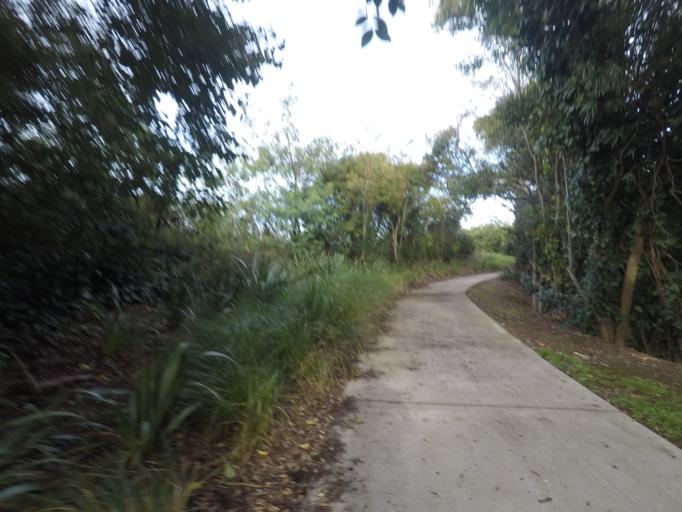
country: NZ
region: Auckland
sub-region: Auckland
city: Mangere
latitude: -36.9469
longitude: 174.8060
